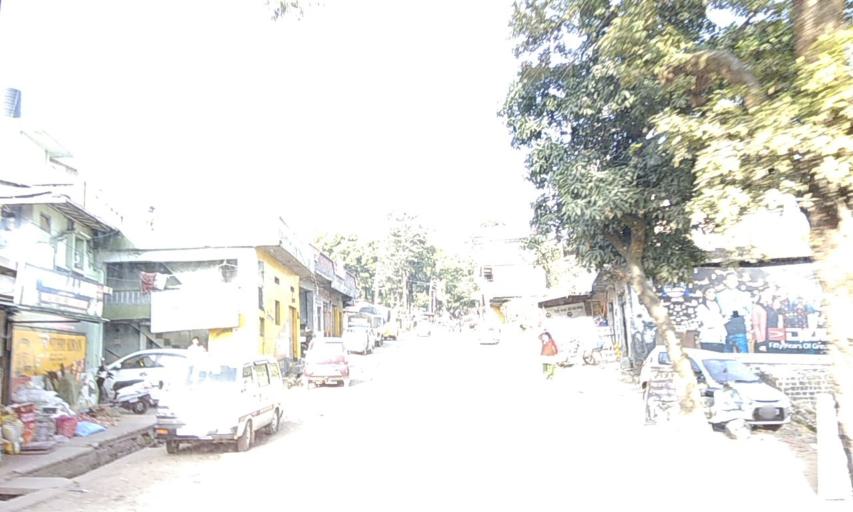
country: IN
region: Himachal Pradesh
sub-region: Kangra
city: Palampur
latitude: 32.0867
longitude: 76.5243
